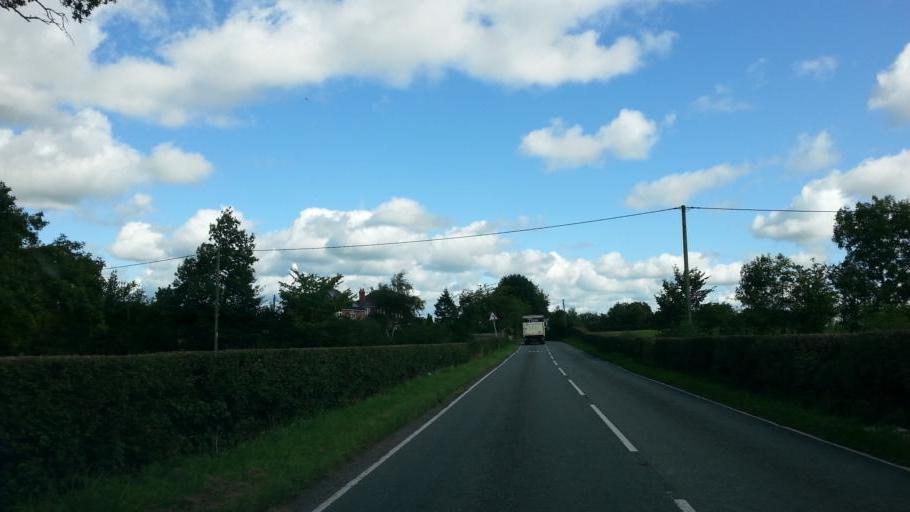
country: GB
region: England
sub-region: Staffordshire
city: Uttoxeter
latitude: 52.8814
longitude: -1.8813
